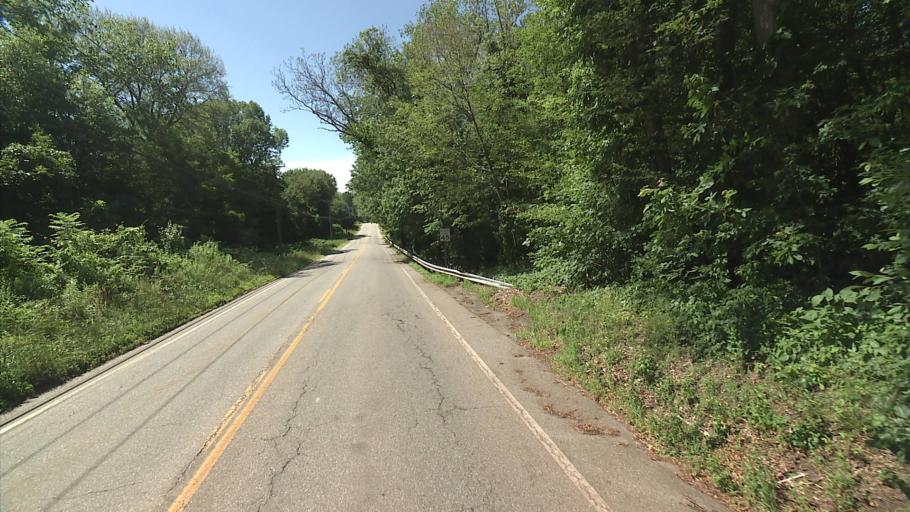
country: US
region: Connecticut
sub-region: Windham County
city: Willimantic
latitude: 41.6683
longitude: -72.2260
